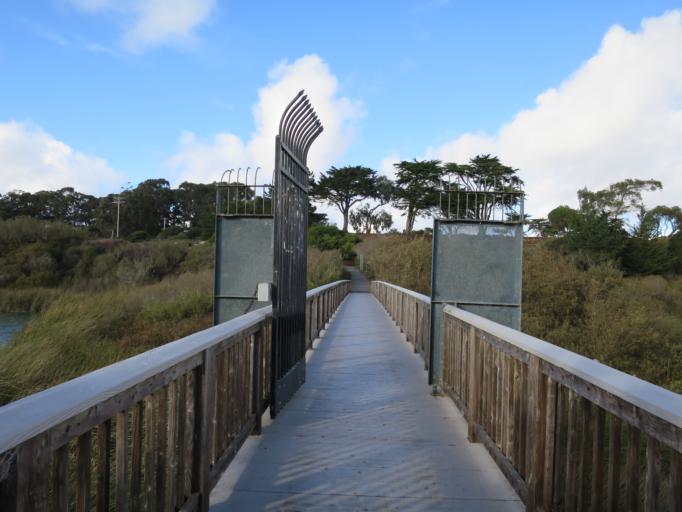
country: US
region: California
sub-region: San Mateo County
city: Daly City
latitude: 37.7271
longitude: -122.4934
